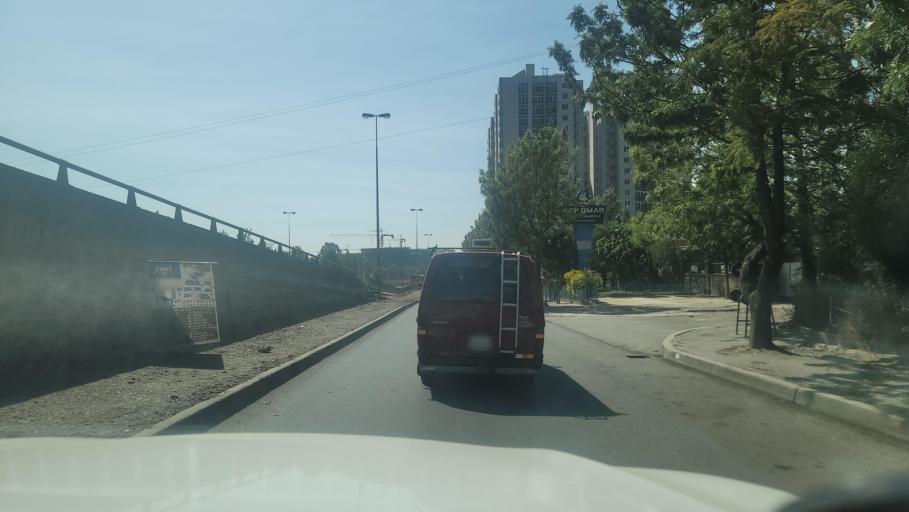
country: ET
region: Adis Abeba
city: Addis Ababa
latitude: 9.0170
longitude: 38.8023
